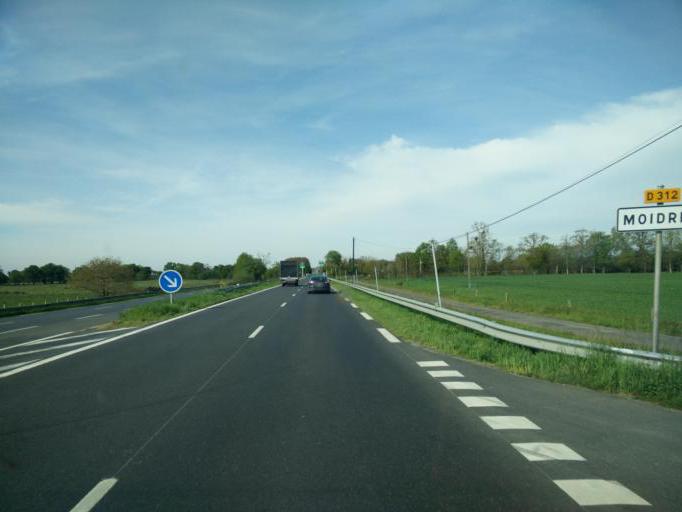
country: FR
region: Lower Normandy
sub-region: Departement de la Manche
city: Pontorson
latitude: 48.5645
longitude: -1.4771
